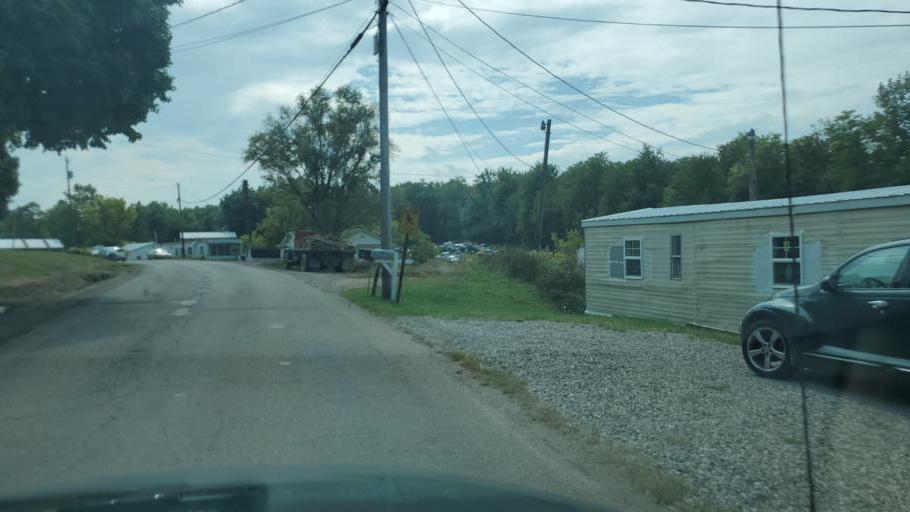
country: US
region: Ohio
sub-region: Muskingum County
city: Zanesville
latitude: 39.9602
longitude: -82.1518
